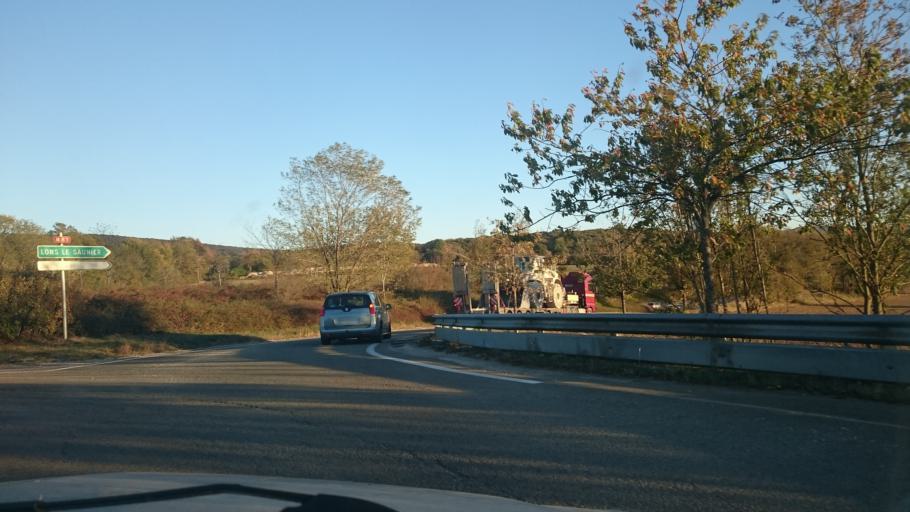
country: FR
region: Franche-Comte
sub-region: Departement du Doubs
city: Quingey
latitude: 47.0813
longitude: 5.8822
